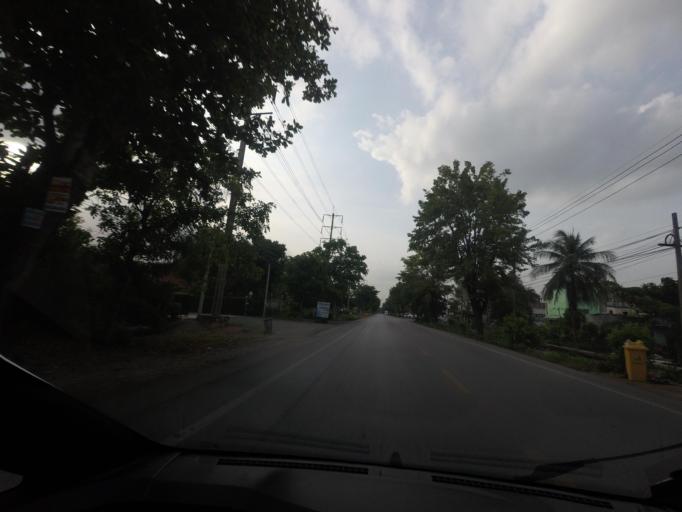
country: TH
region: Bangkok
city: Nong Chok
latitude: 13.8922
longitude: 100.8635
